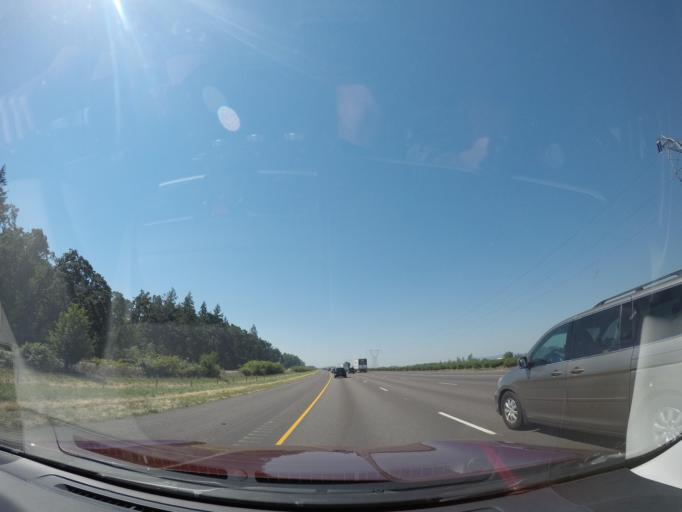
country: US
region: Oregon
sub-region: Marion County
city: Gervais
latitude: 45.0723
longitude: -122.9607
